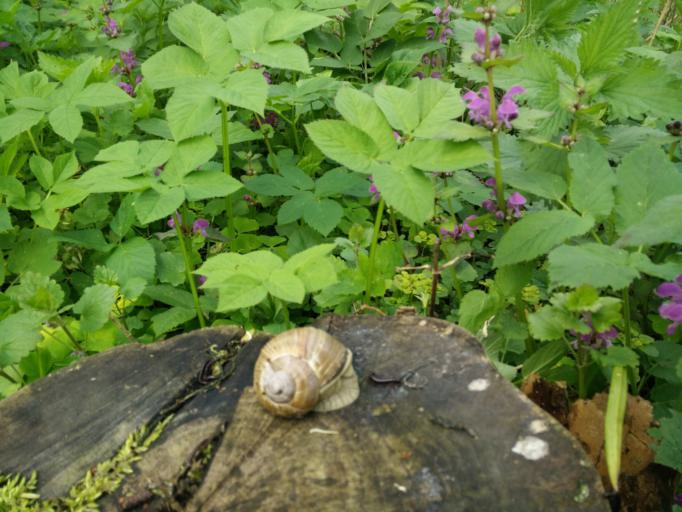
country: LT
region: Vilnius County
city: Rasos
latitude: 54.6902
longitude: 25.3531
